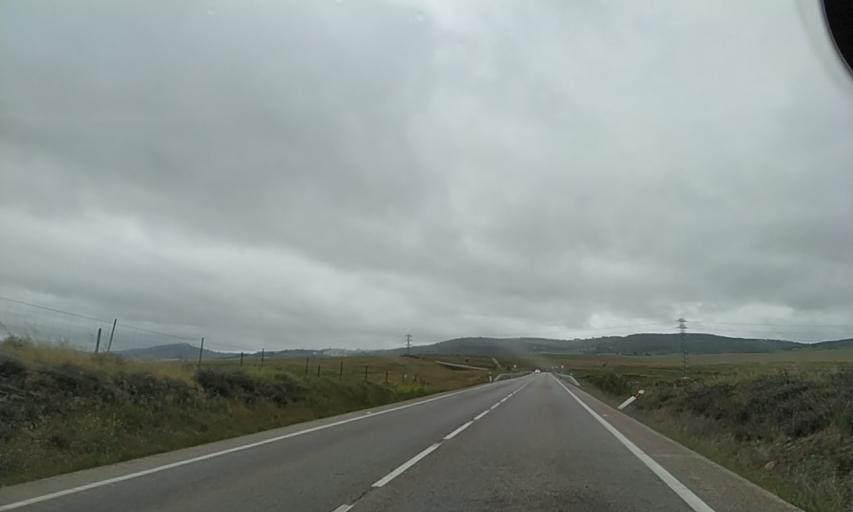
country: ES
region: Extremadura
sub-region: Provincia de Caceres
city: Casar de Caceres
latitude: 39.5220
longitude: -6.3982
